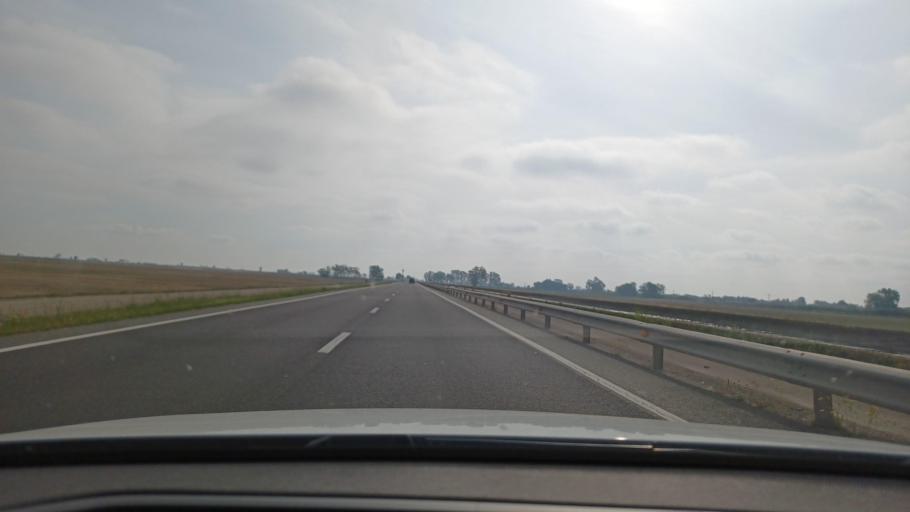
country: ES
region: Catalonia
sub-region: Provincia de Tarragona
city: Amposta
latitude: 40.7180
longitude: 0.6395
